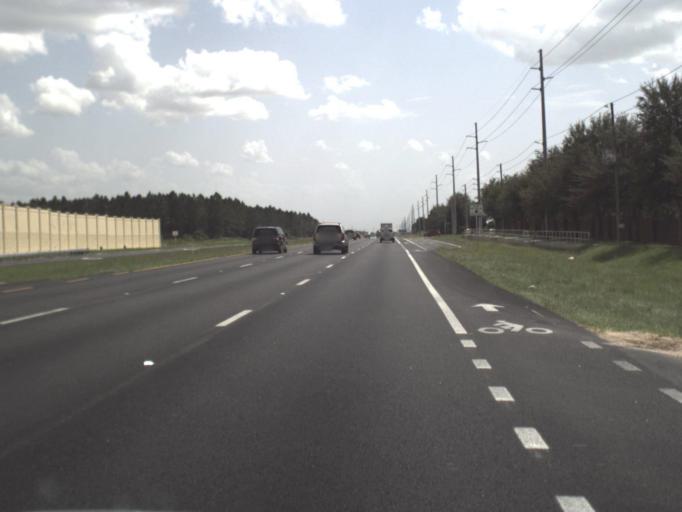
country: US
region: Florida
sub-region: Lake County
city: Four Corners
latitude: 28.2666
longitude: -81.6607
